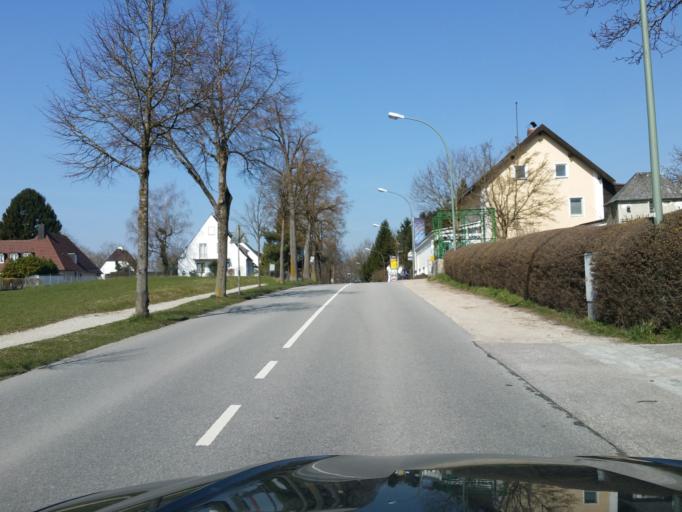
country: DE
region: Bavaria
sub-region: Lower Bavaria
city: Landshut
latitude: 48.5241
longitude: 12.1685
